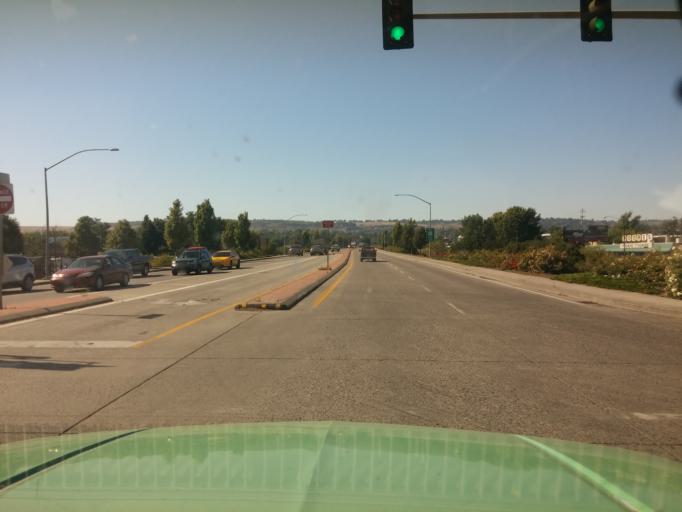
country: US
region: Idaho
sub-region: Nez Perce County
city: Lewiston
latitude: 46.4236
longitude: -117.0004
